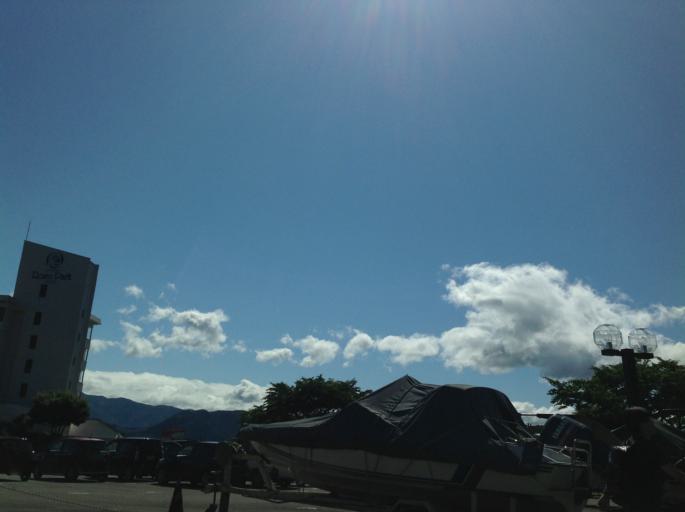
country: JP
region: Akita
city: Kakunodatemachi
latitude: 39.7125
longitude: 140.6337
